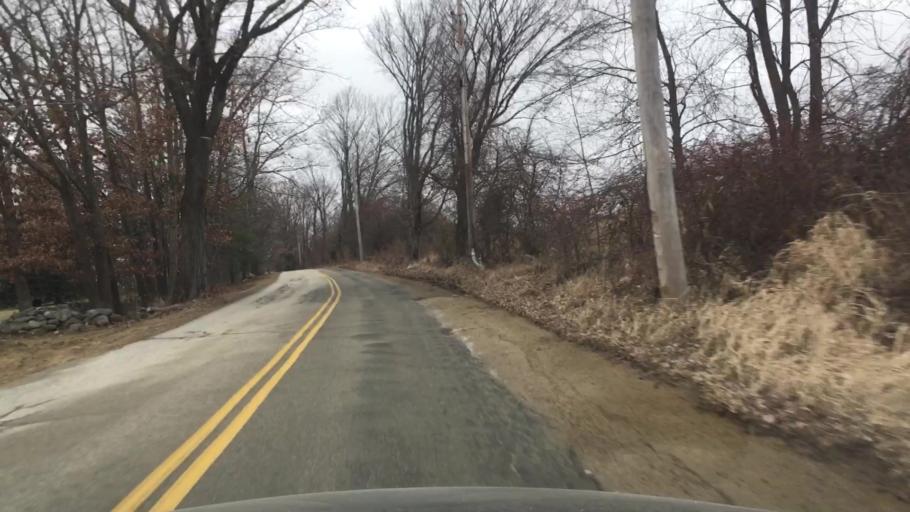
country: US
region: New Hampshire
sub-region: Hillsborough County
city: Mont Vernon
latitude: 42.9327
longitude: -71.6080
